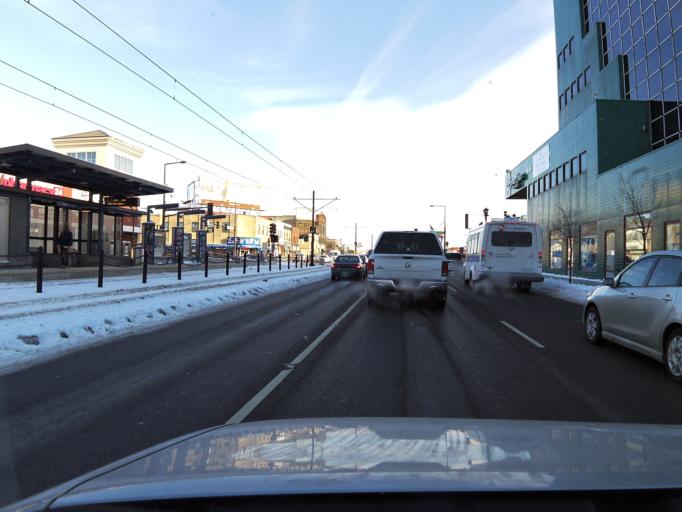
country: US
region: Minnesota
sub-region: Ramsey County
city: Falcon Heights
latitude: 44.9555
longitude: -93.1678
